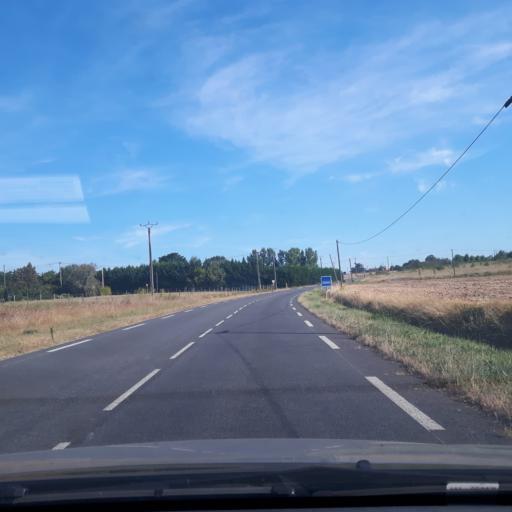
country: FR
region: Midi-Pyrenees
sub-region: Departement de la Haute-Garonne
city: Villeneuve-les-Bouloc
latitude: 43.7702
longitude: 1.4387
